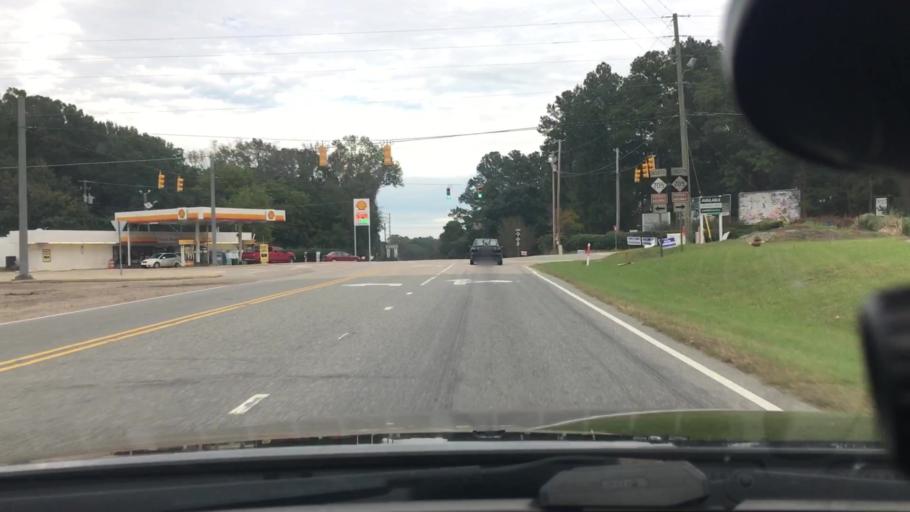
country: US
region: North Carolina
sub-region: Moore County
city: Robbins
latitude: 35.4042
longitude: -79.5755
